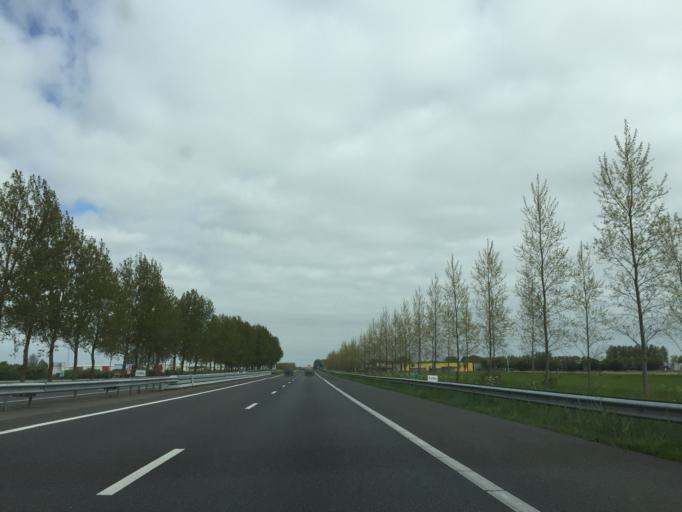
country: NL
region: North Holland
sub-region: Gemeente Medemblik
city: Opperdoes
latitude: 52.8312
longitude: 5.0218
